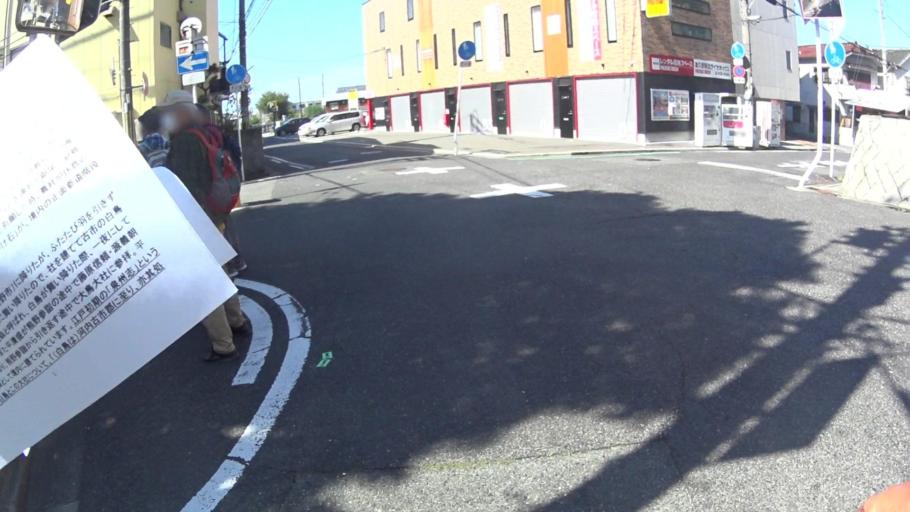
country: JP
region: Osaka
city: Takaishi
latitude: 34.5353
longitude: 135.4785
